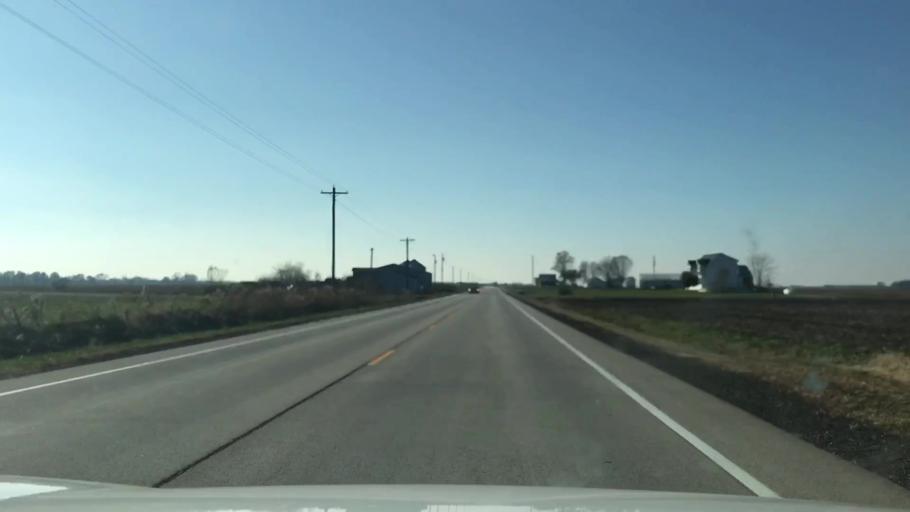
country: US
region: Illinois
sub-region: Washington County
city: Okawville
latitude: 38.4424
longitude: -89.5035
